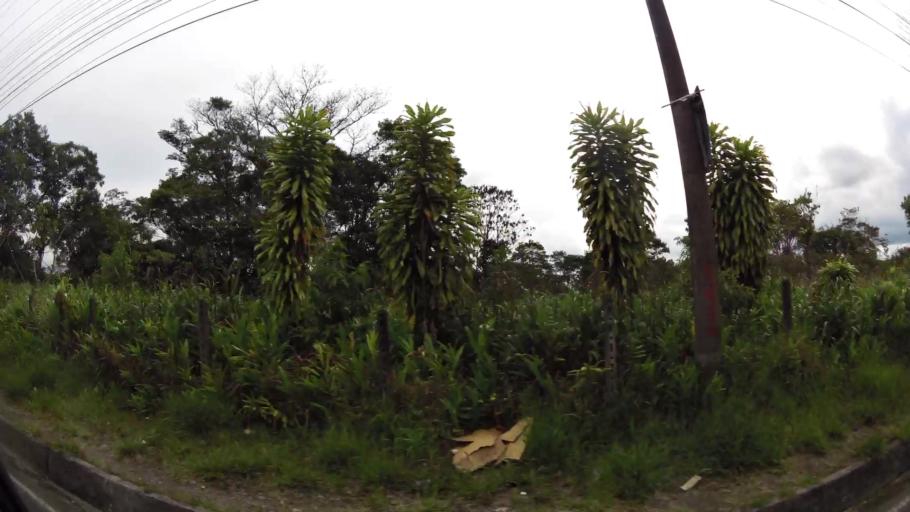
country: EC
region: Pastaza
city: Puyo
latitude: -1.5072
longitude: -78.0315
